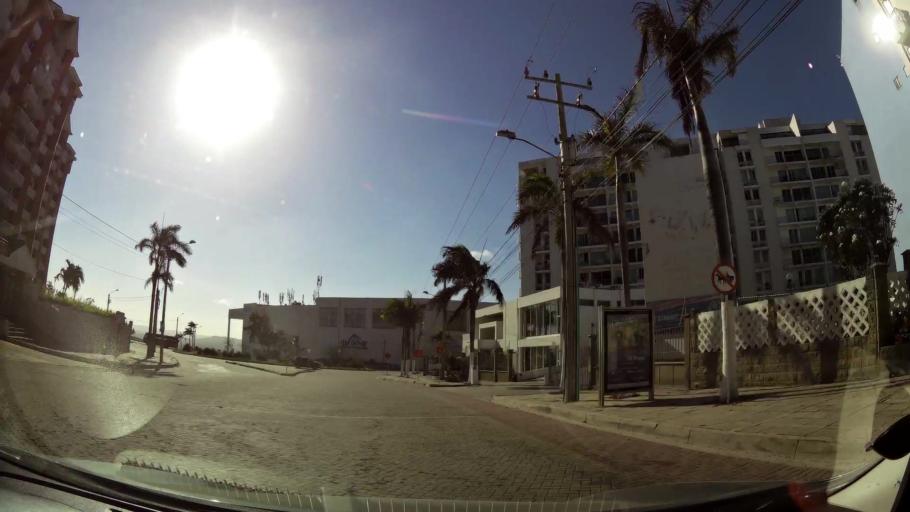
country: CO
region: Atlantico
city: Barranquilla
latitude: 11.0034
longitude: -74.8339
